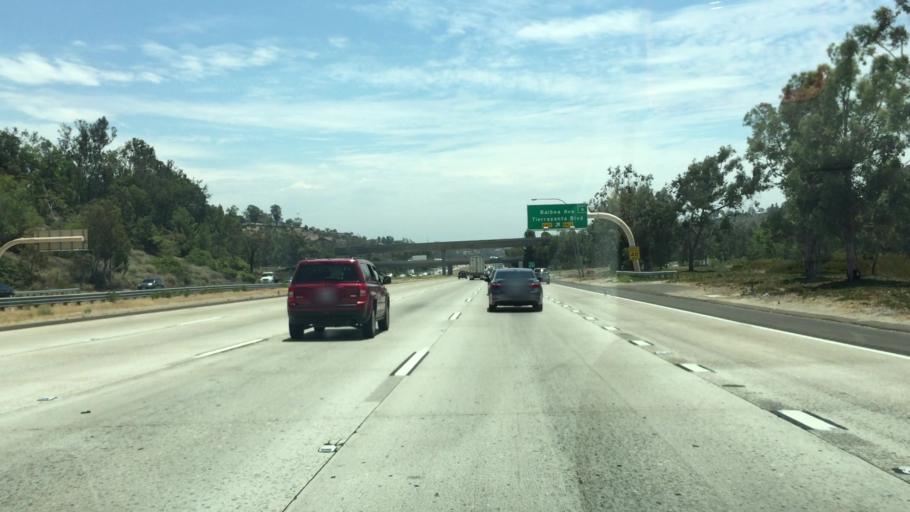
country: US
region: California
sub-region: San Diego County
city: La Mesa
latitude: 32.8274
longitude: -117.1178
